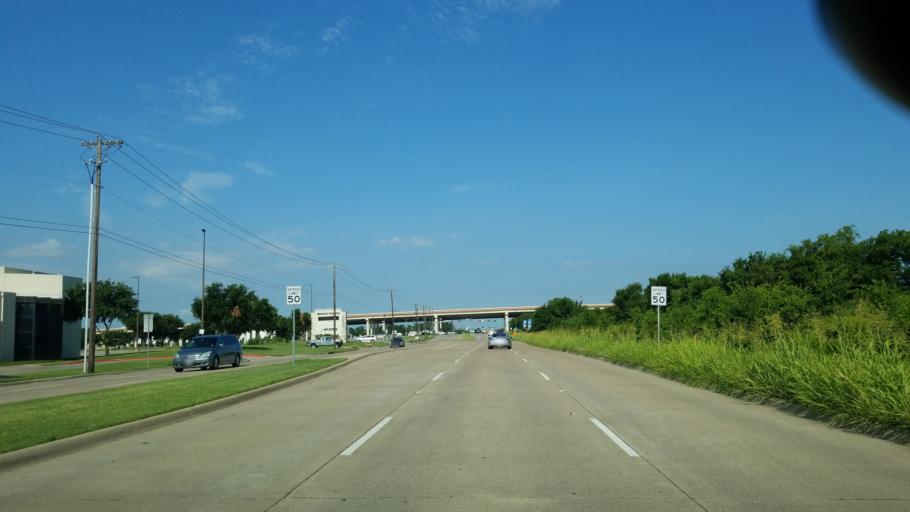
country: US
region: Texas
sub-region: Dallas County
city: Carrollton
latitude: 32.9522
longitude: -96.9213
